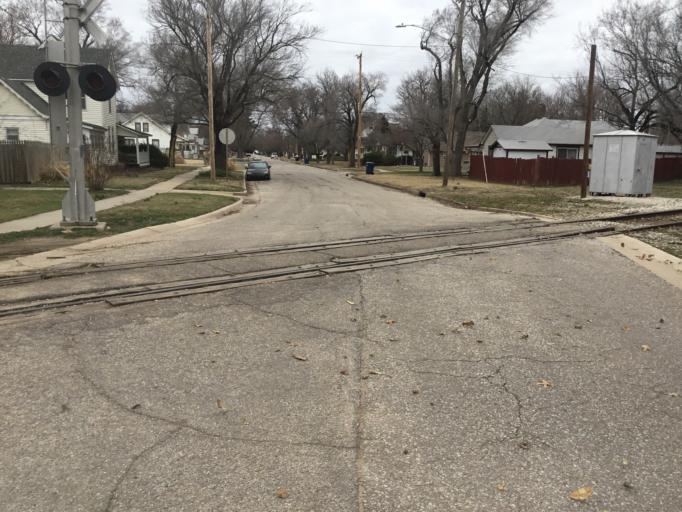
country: US
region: Kansas
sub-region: Sedgwick County
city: Wichita
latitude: 37.6816
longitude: -97.3641
